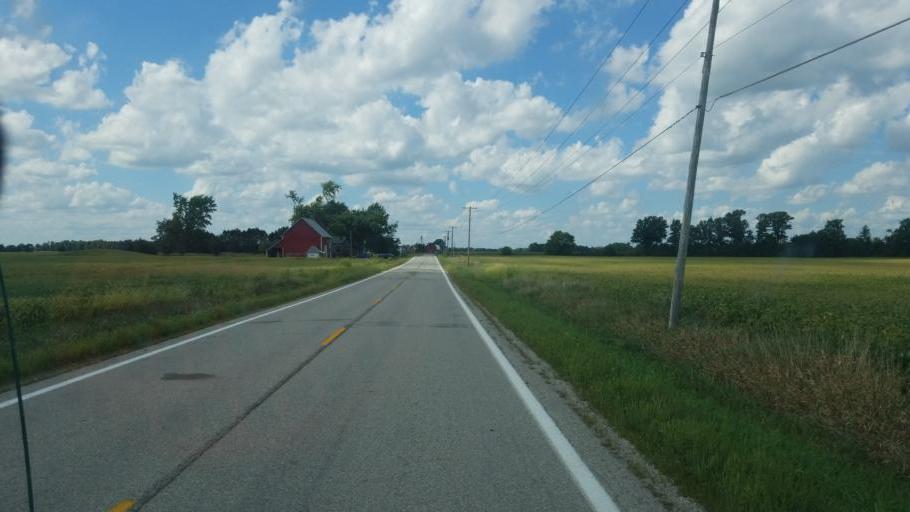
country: US
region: Ohio
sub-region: Union County
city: Richwood
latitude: 40.3773
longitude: -83.2742
